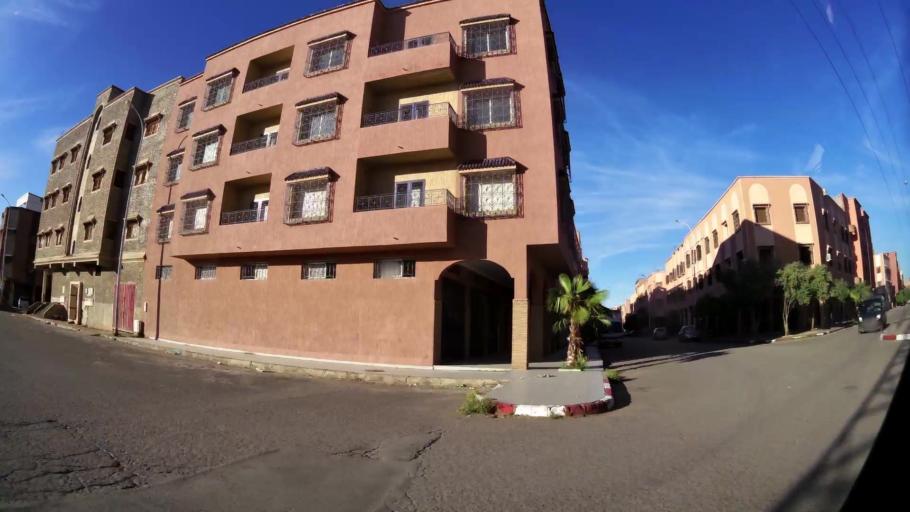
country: MA
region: Marrakech-Tensift-Al Haouz
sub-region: Marrakech
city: Marrakesh
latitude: 31.6152
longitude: -8.0649
